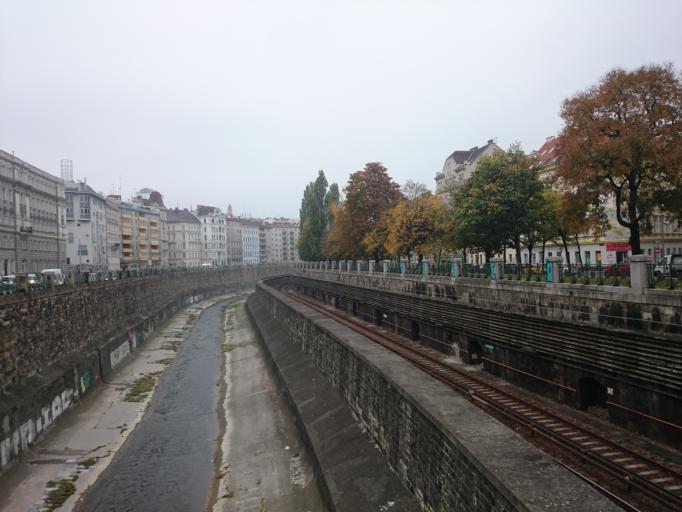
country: AT
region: Vienna
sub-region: Wien Stadt
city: Vienna
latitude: 48.1930
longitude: 16.3545
